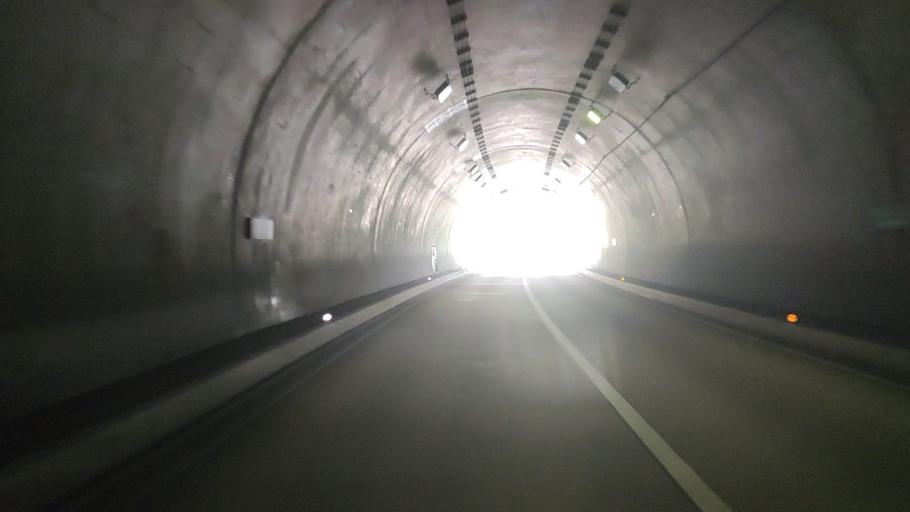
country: JP
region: Wakayama
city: Shingu
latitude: 33.8599
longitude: 135.8522
